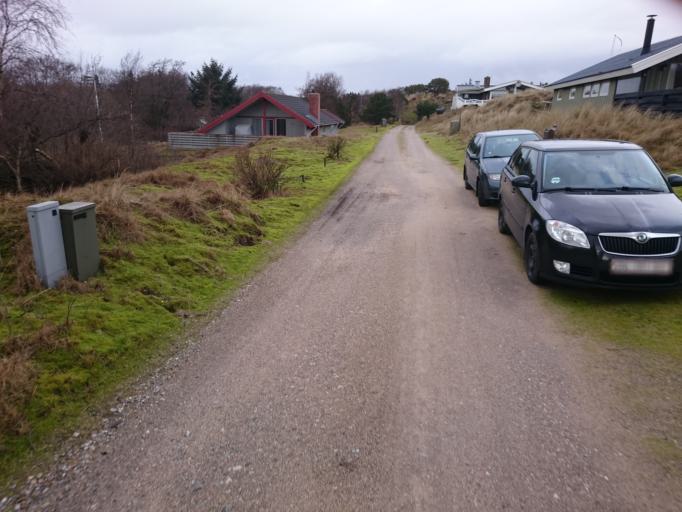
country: DK
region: South Denmark
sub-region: Fano Kommune
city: Nordby
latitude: 55.4362
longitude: 8.3792
